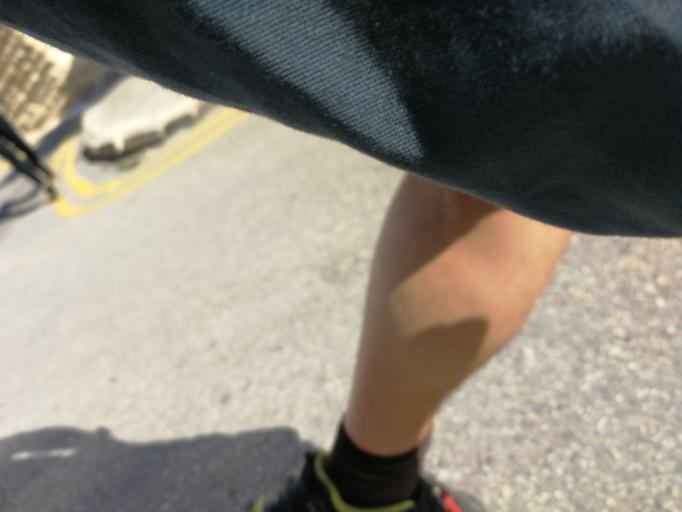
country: MT
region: Saint Julian
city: San Giljan
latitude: 35.9182
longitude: 14.4876
